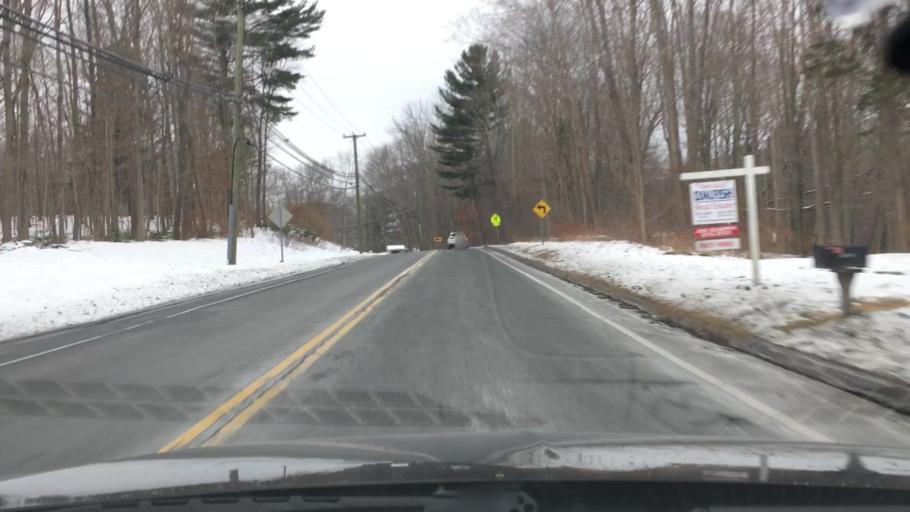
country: US
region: Connecticut
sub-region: Tolland County
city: Tolland
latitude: 41.8509
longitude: -72.3303
